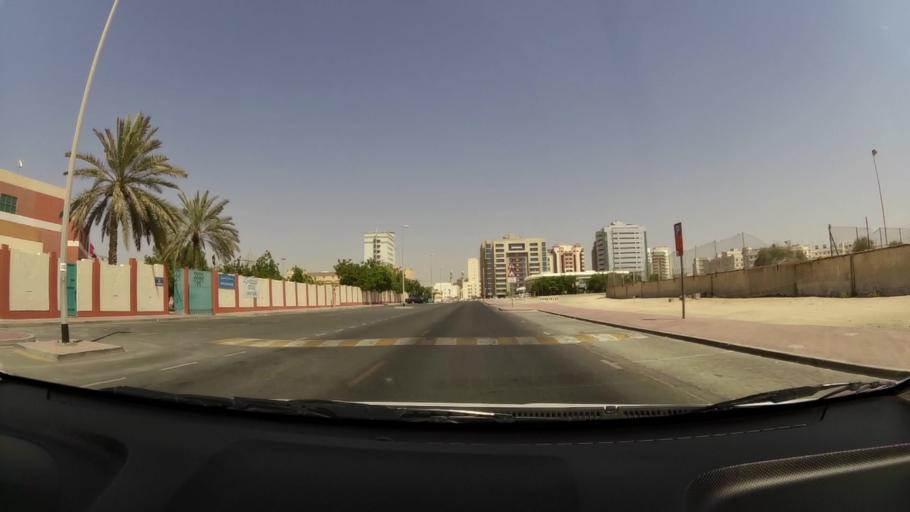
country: AE
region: Ash Shariqah
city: Sharjah
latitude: 25.2782
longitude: 55.3671
